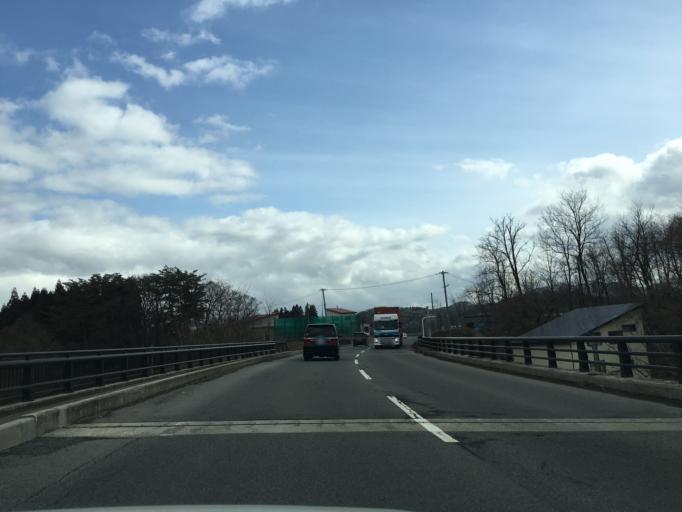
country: JP
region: Akita
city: Hanawa
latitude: 40.2332
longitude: 140.7006
